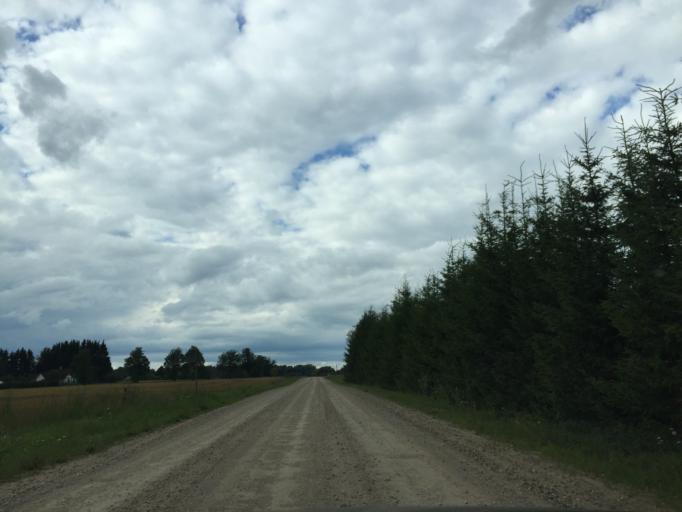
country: LV
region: Malpils
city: Malpils
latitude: 56.9534
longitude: 24.9883
